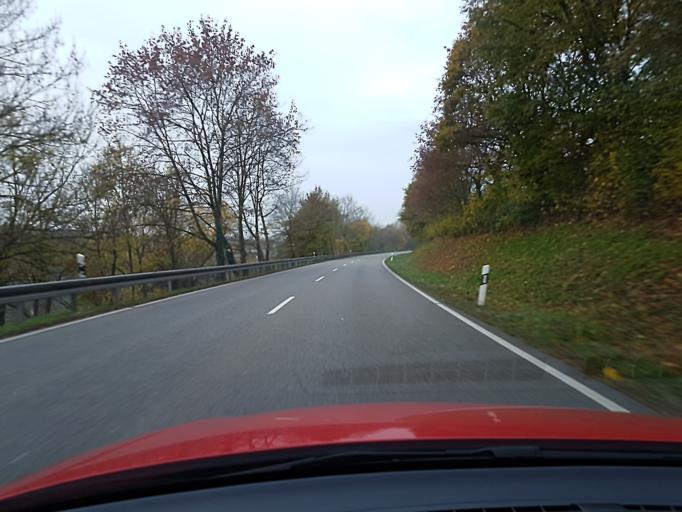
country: DE
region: Baden-Wuerttemberg
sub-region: Regierungsbezirk Stuttgart
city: Walheim
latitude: 49.0103
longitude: 9.1571
